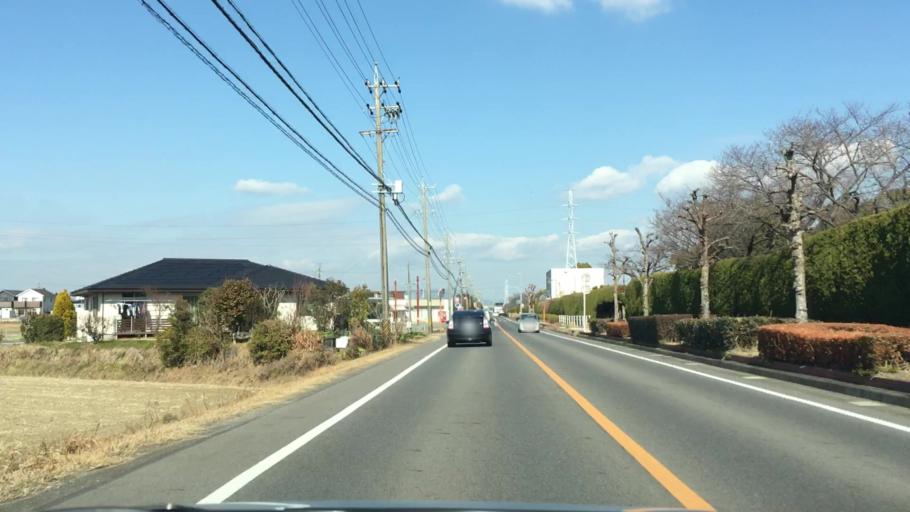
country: JP
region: Aichi
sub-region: Toyota-shi
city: Toyota
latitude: 35.0221
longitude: 137.1270
